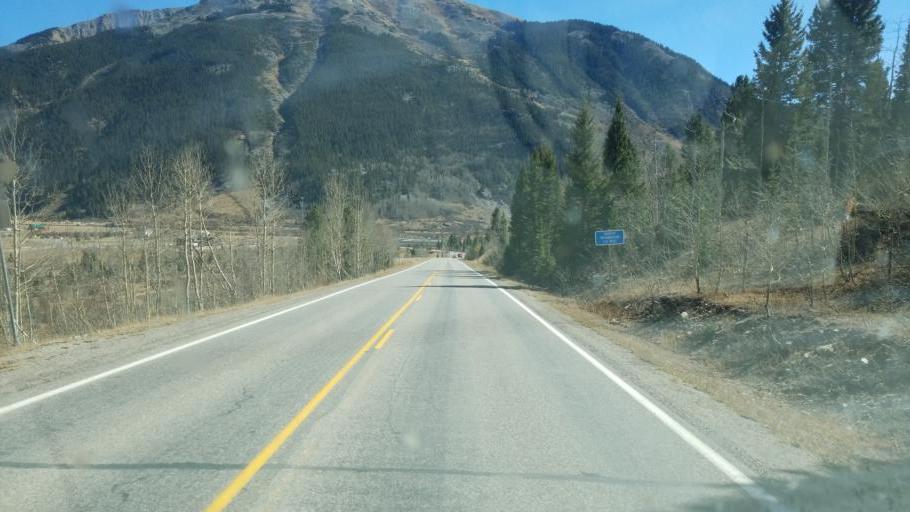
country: US
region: Colorado
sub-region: San Juan County
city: Silverton
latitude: 37.8057
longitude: -107.6784
